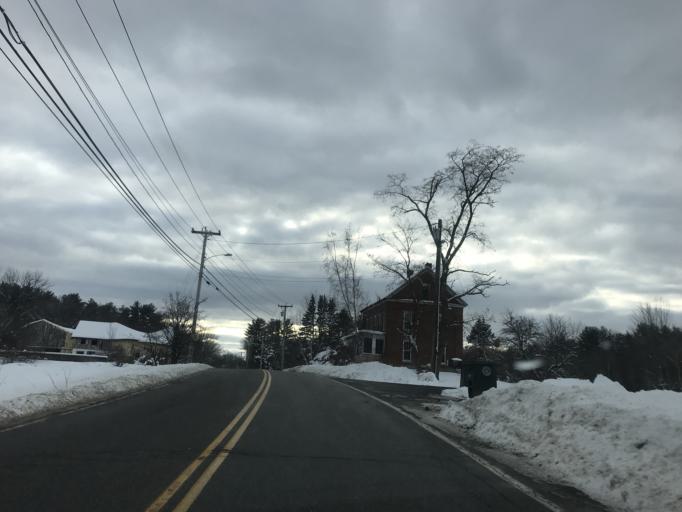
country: US
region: Maine
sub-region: Cumberland County
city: Westbrook
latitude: 43.7172
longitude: -70.3294
